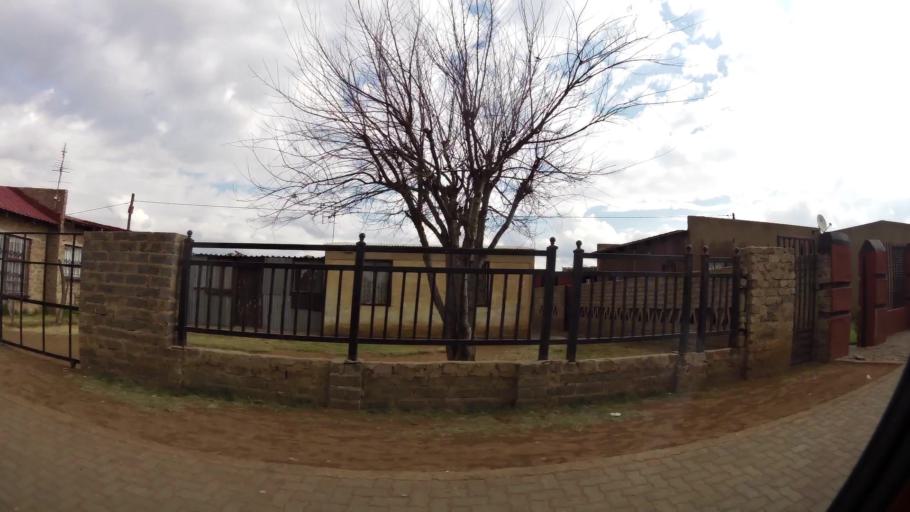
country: ZA
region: Gauteng
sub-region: Sedibeng District Municipality
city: Vanderbijlpark
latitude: -26.6995
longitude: 27.8020
